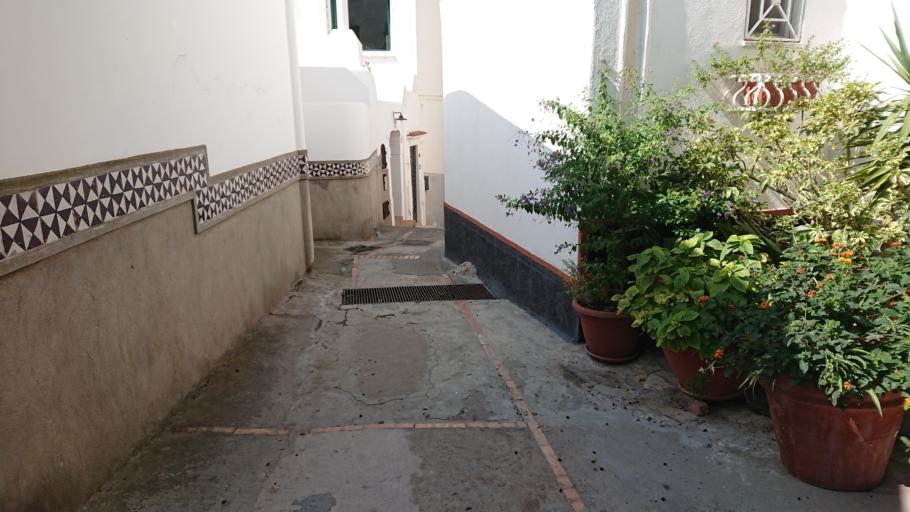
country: IT
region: Campania
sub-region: Provincia di Napoli
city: Anacapri
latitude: 40.5547
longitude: 14.2158
